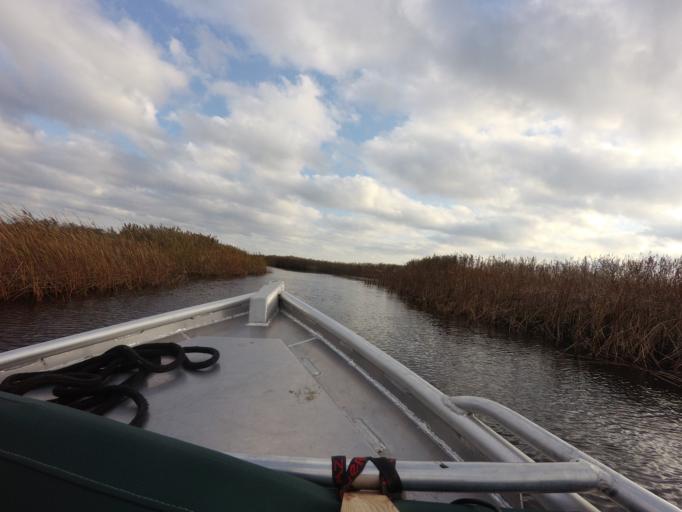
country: NL
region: Overijssel
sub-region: Gemeente Steenwijkerland
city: Blokzijl
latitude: 52.7498
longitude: 5.9652
